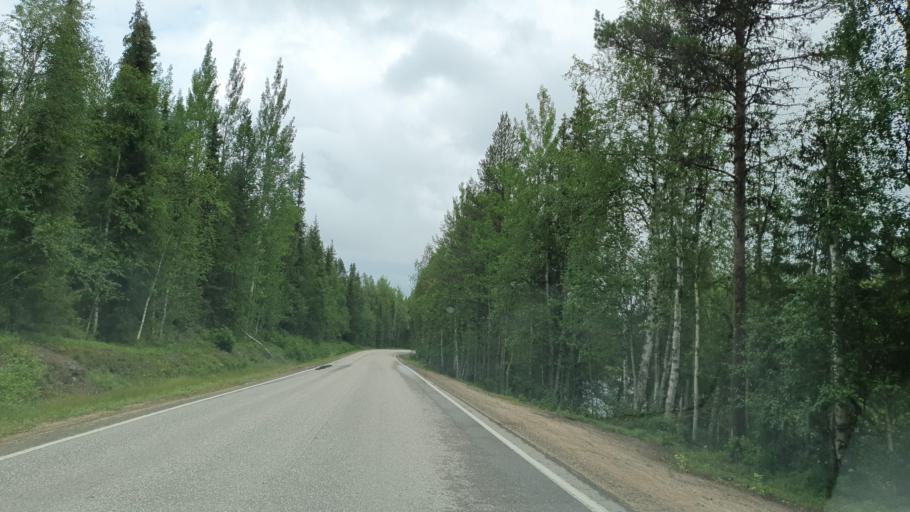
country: FI
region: Lapland
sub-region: Tunturi-Lappi
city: Kolari
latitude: 67.5848
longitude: 24.0859
